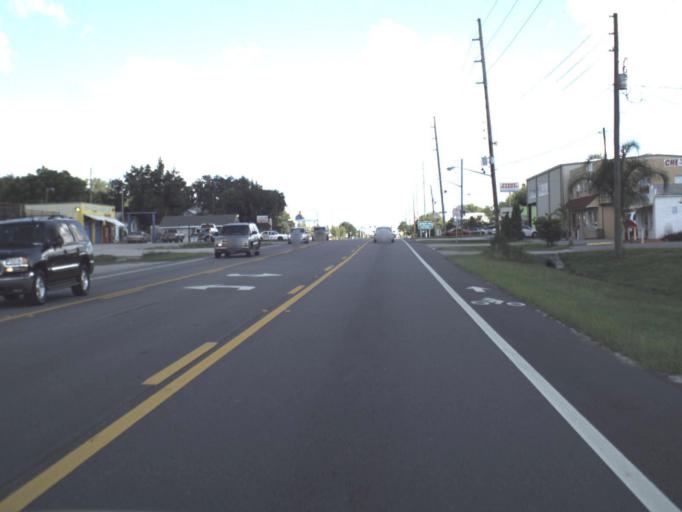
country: US
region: Florida
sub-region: Polk County
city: Haines City
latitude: 28.1091
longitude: -81.6180
